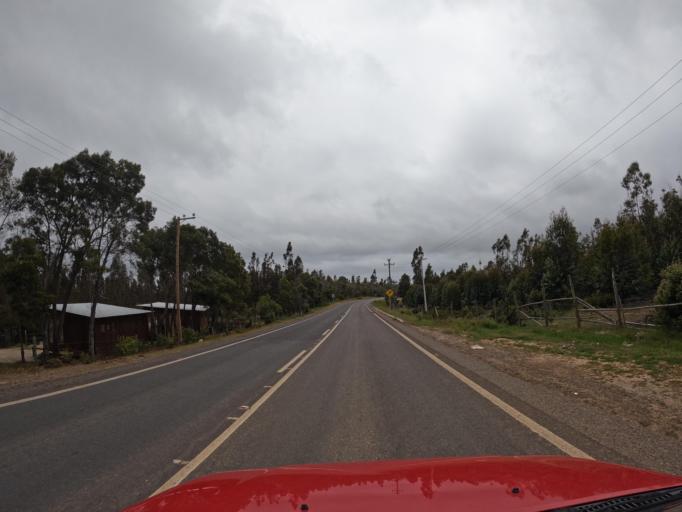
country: CL
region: O'Higgins
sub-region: Provincia de Colchagua
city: Santa Cruz
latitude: -34.5040
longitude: -72.0060
